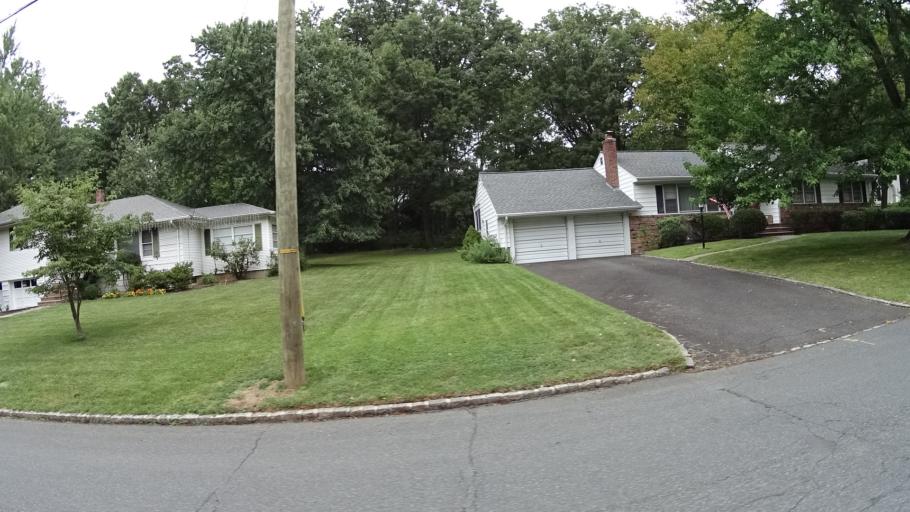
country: US
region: New Jersey
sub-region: Union County
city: New Providence
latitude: 40.7127
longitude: -74.3925
